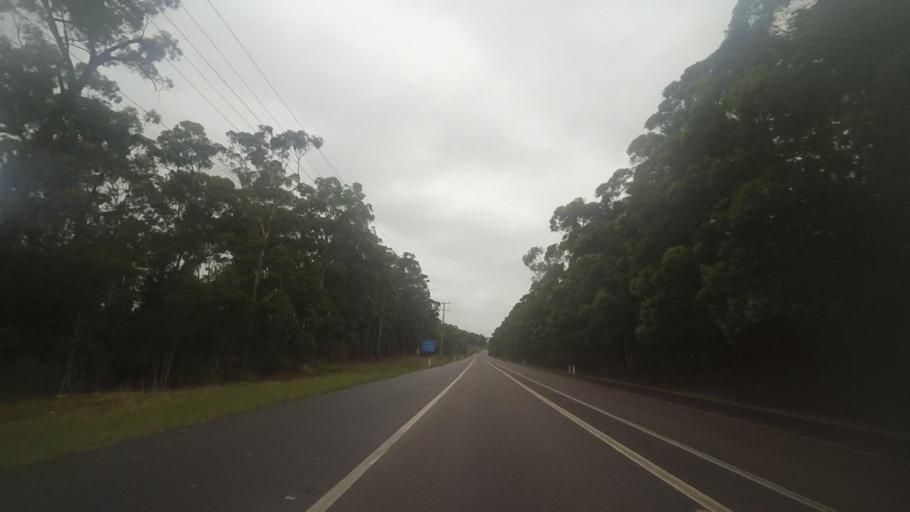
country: AU
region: New South Wales
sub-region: Port Stephens Shire
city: Port Stephens
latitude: -32.6407
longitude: 151.9904
